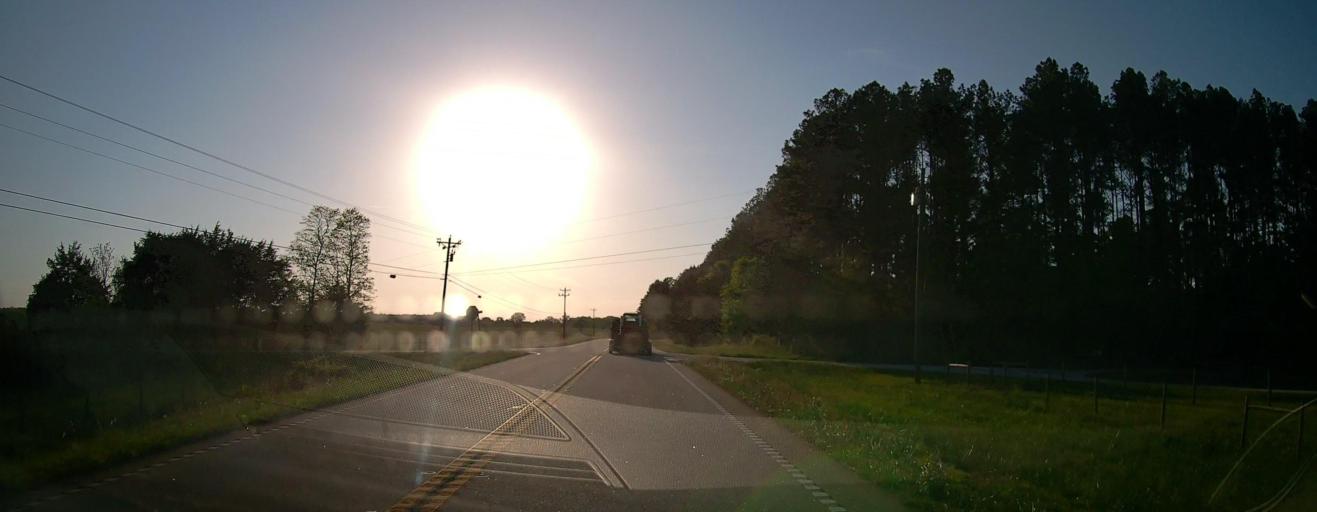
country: US
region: Georgia
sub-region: Walton County
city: Social Circle
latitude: 33.5340
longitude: -83.7155
